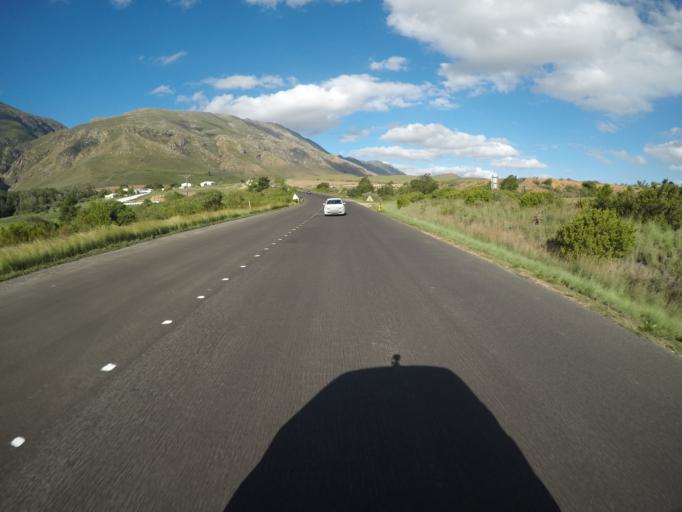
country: ZA
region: Western Cape
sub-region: Cape Winelands District Municipality
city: Ashton
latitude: -33.8733
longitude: 20.1542
